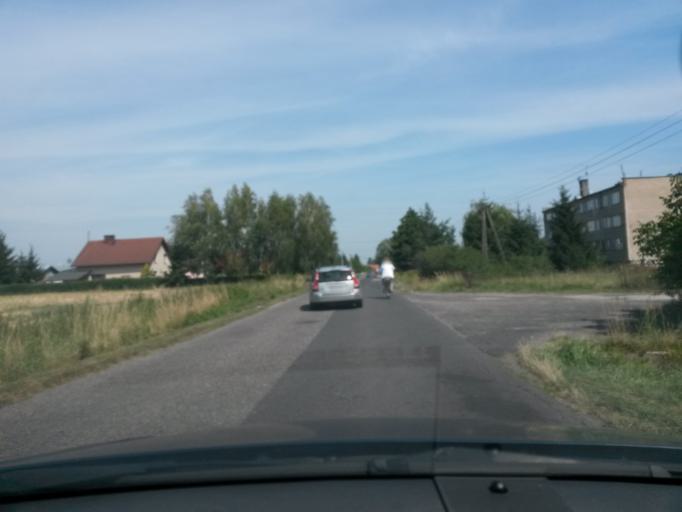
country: PL
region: Lower Silesian Voivodeship
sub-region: Powiat legnicki
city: Prochowice
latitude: 51.2550
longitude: 16.3632
